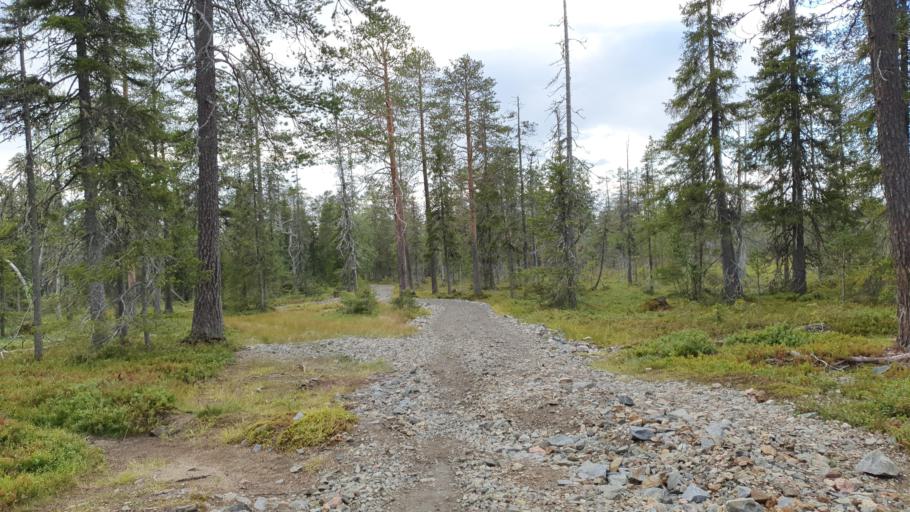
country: FI
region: Lapland
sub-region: Tunturi-Lappi
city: Kolari
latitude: 67.6186
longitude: 24.2317
